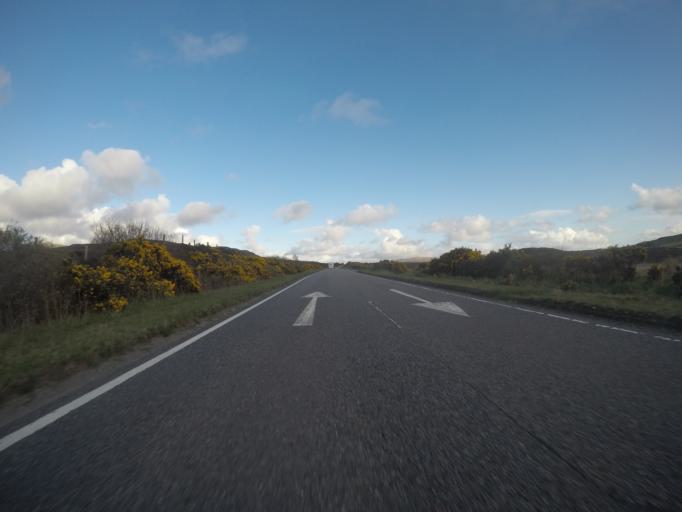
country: GB
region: Scotland
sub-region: Highland
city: Portree
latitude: 57.4728
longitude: -6.2960
